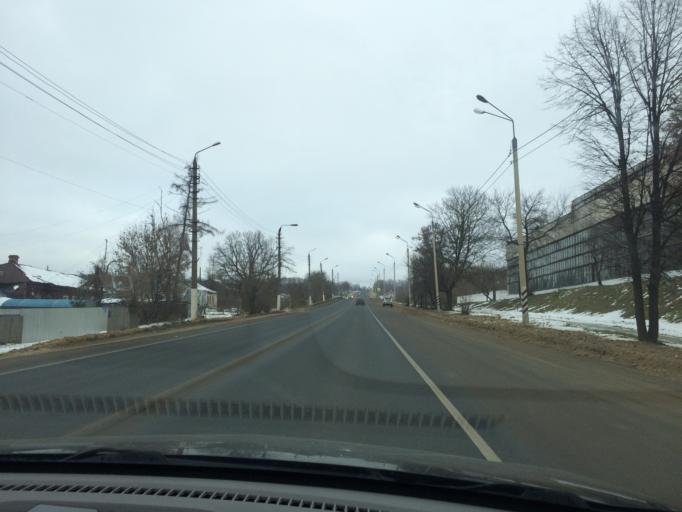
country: RU
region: Tula
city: Plavsk
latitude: 53.7145
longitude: 37.2968
